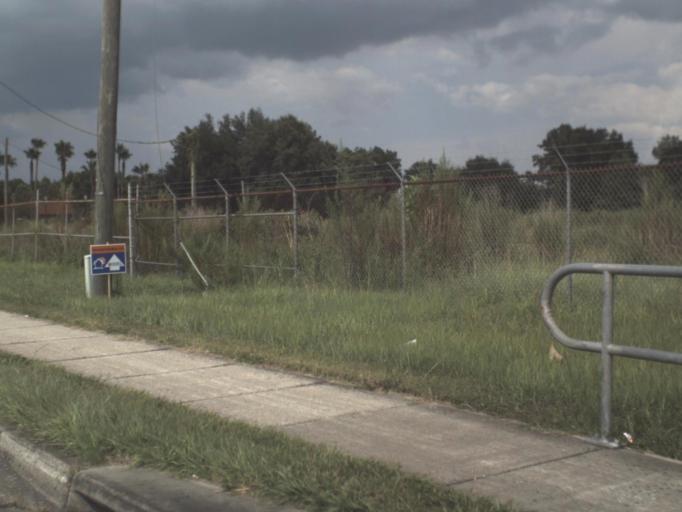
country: US
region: Florida
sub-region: Pasco County
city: Land O' Lakes
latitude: 28.2071
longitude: -82.4623
